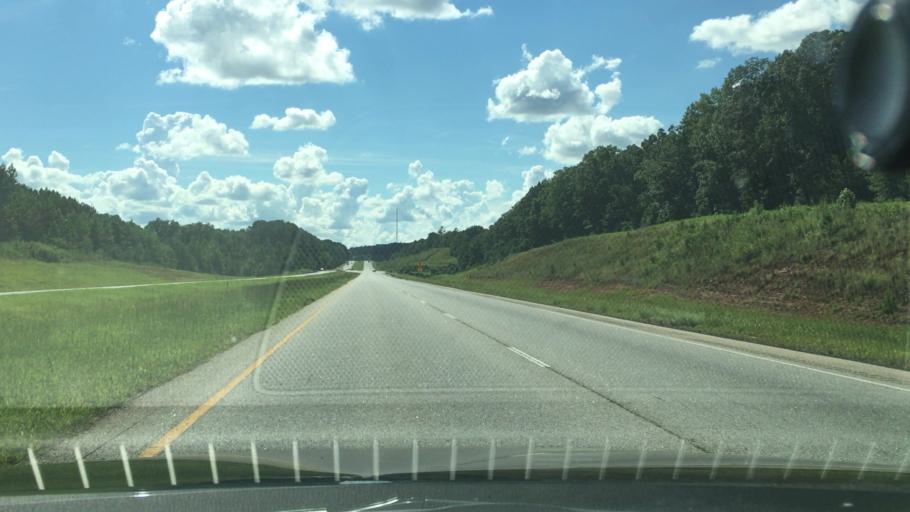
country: US
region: Georgia
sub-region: Spalding County
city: East Griffin
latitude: 33.2369
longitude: -84.1854
